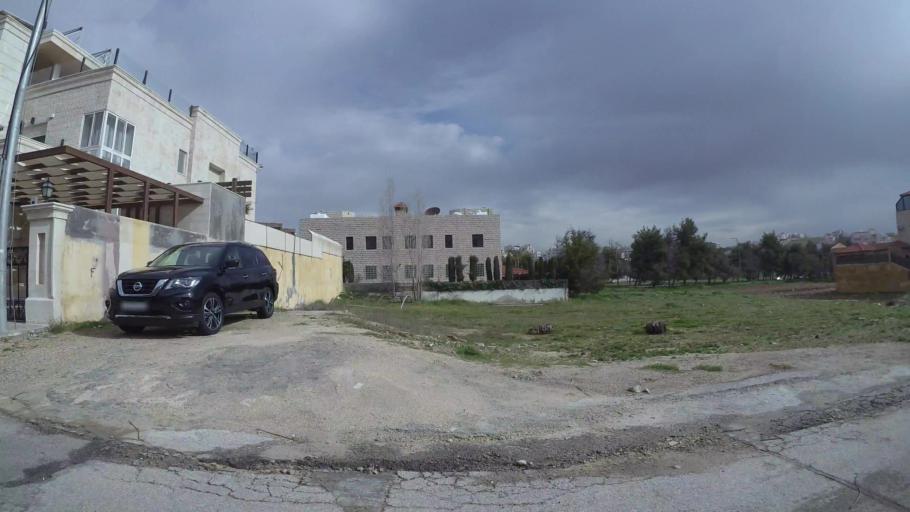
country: JO
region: Amman
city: Wadi as Sir
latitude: 31.9918
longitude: 35.8260
